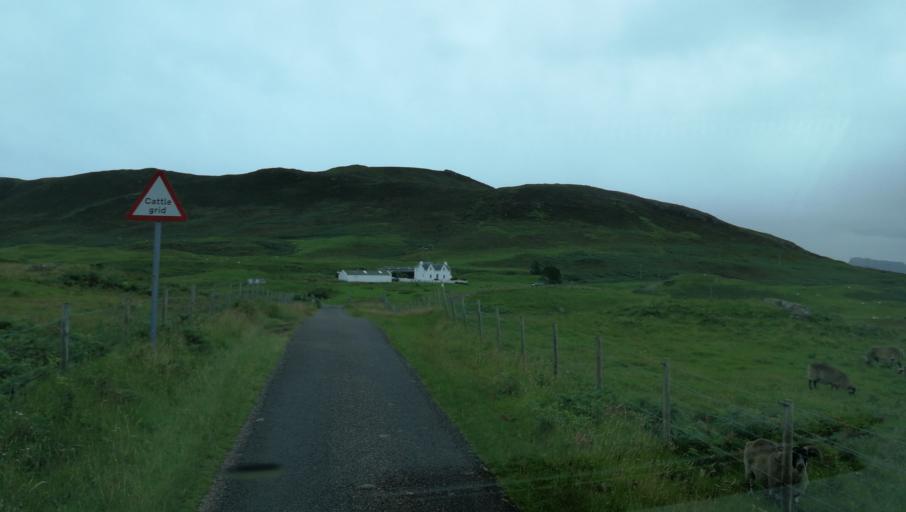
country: GB
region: Scotland
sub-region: Argyll and Bute
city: Isle Of Mull
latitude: 56.7246
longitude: -6.2029
